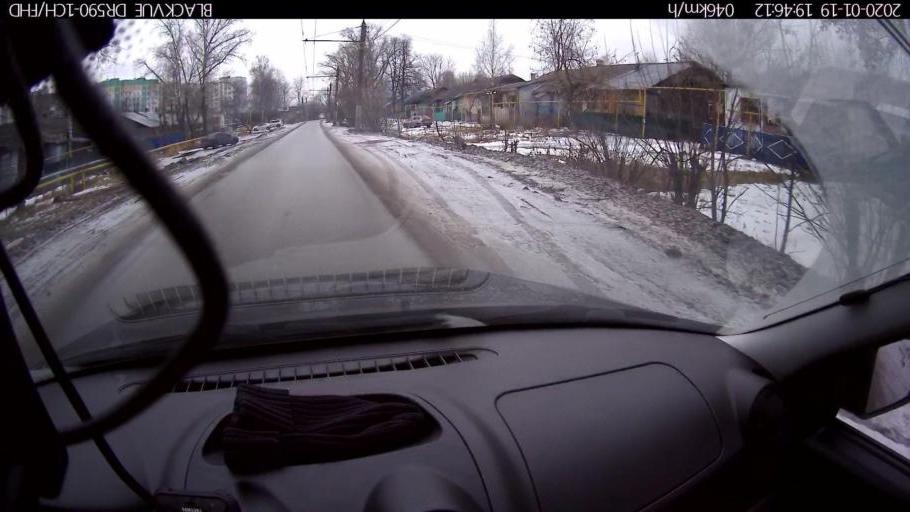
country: RU
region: Nizjnij Novgorod
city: Nizhniy Novgorod
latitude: 56.2915
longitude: 43.9087
